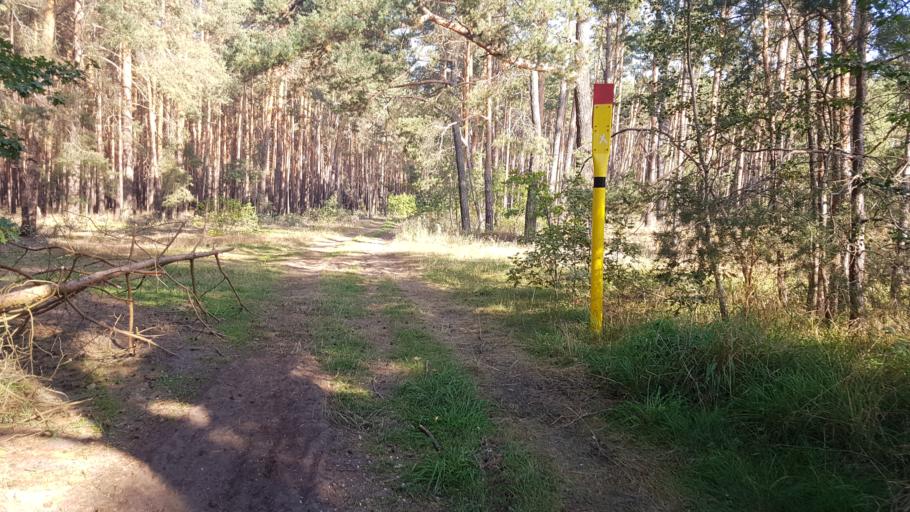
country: DE
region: Brandenburg
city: Finsterwalde
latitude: 51.6474
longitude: 13.6785
